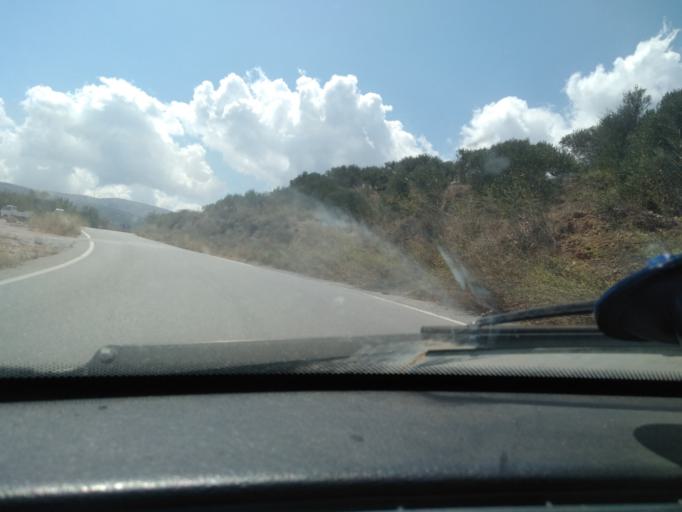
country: GR
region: Crete
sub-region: Nomos Lasithiou
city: Siteia
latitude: 35.1355
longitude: 26.0751
